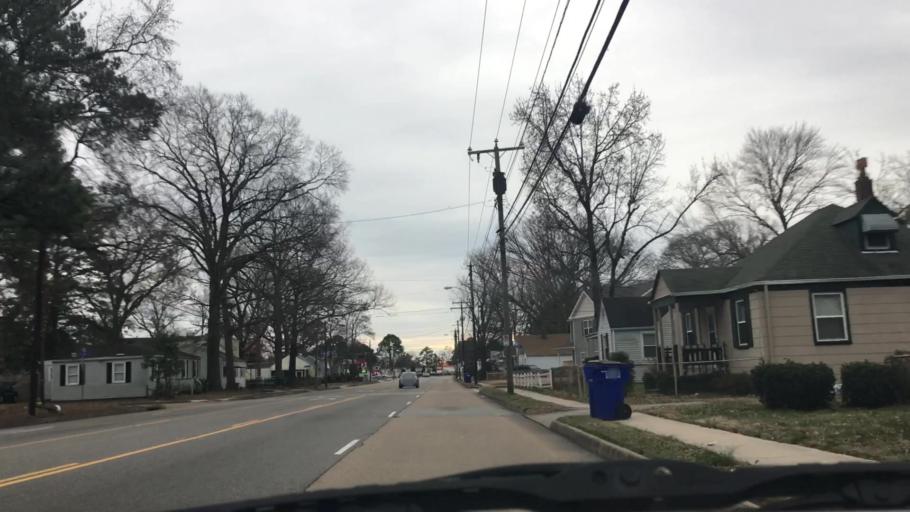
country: US
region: Virginia
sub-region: City of Norfolk
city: Norfolk
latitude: 36.8739
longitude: -76.2326
